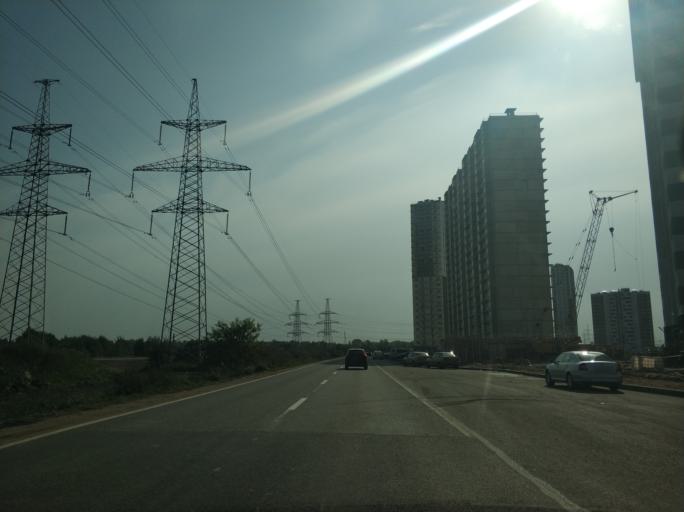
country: RU
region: St.-Petersburg
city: Krasnogvargeisky
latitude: 60.0131
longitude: 30.4791
